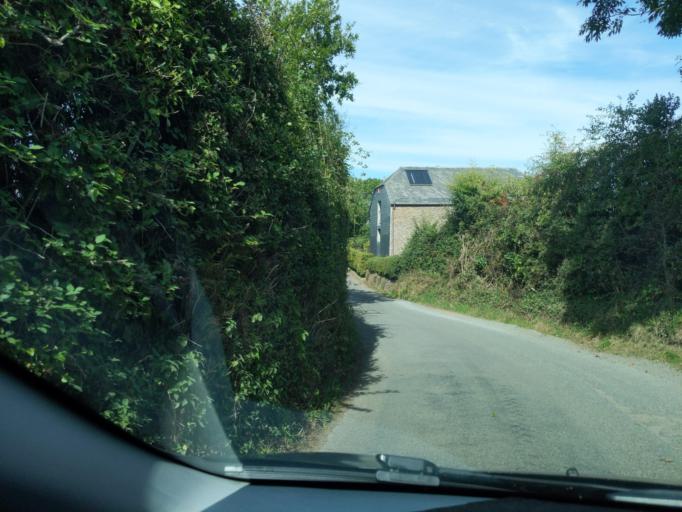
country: GB
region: England
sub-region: Cornwall
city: Torpoint
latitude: 50.3580
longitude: -4.2328
